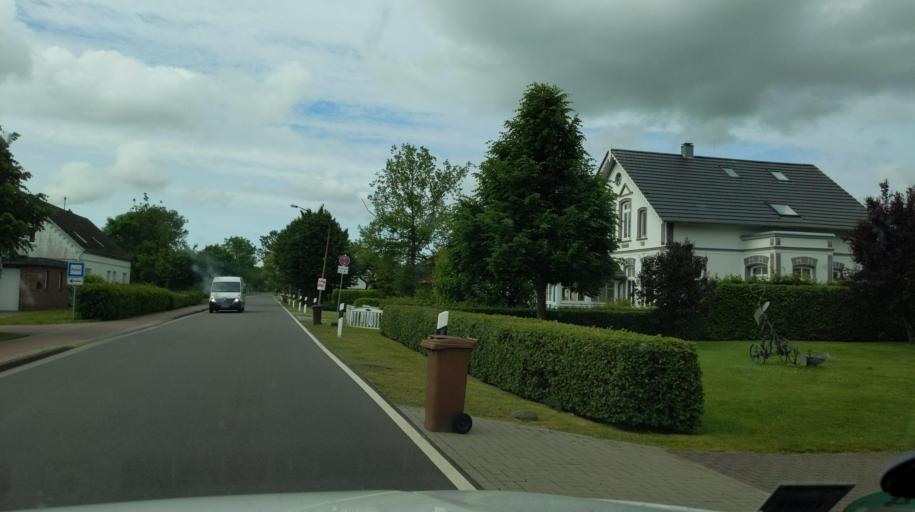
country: DE
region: Lower Saxony
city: Butjadingen
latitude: 53.5711
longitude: 8.3677
